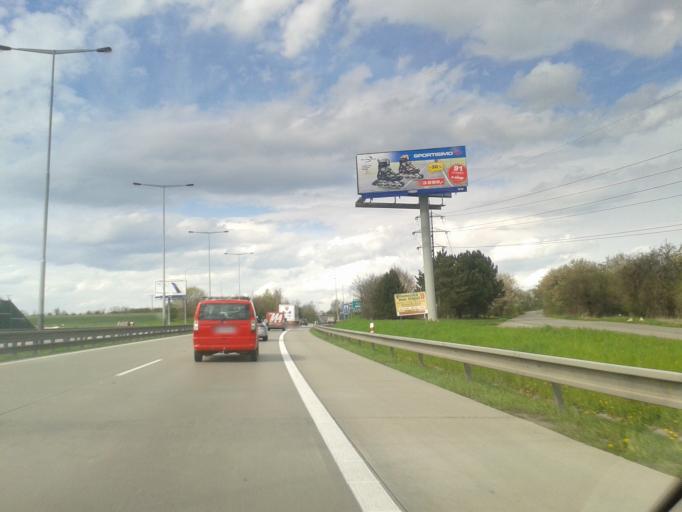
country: CZ
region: Central Bohemia
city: Rudna
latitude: 50.0384
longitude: 14.2716
